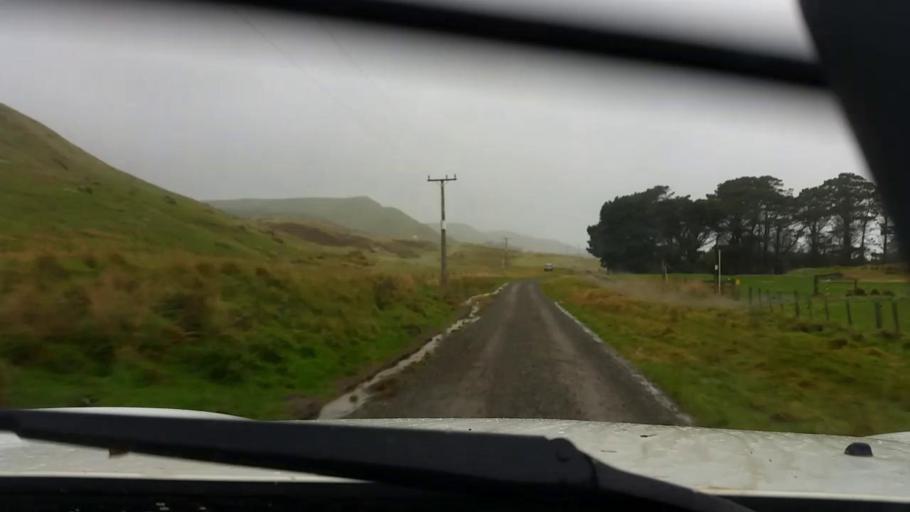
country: NZ
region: Wellington
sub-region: Masterton District
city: Masterton
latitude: -41.2540
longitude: 175.9107
